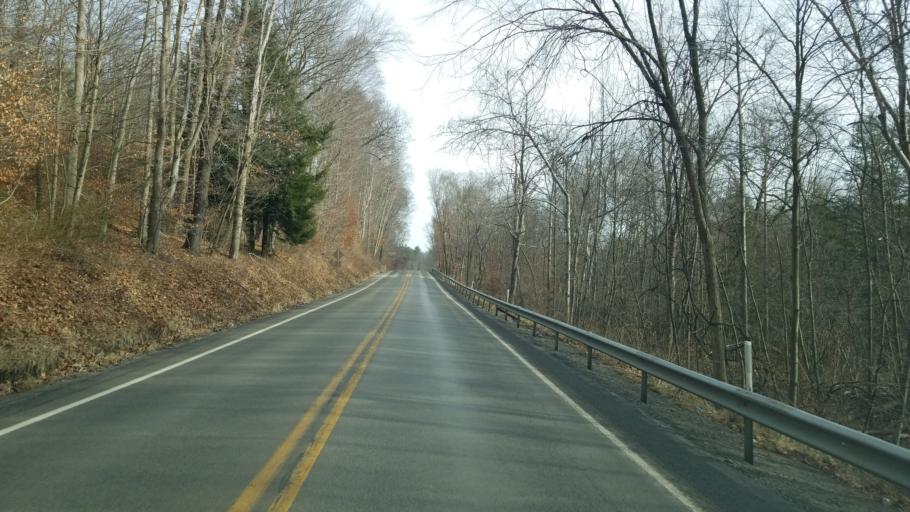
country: US
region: Pennsylvania
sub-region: Indiana County
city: Johnsonburg
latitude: 40.8148
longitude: -78.8336
